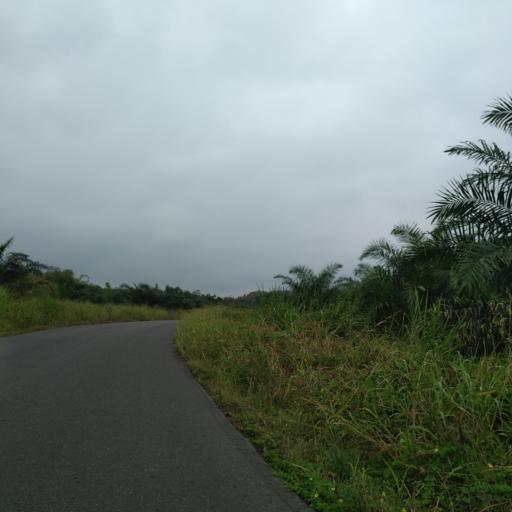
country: EC
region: Los Rios
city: Quevedo
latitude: -0.9706
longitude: -79.3528
